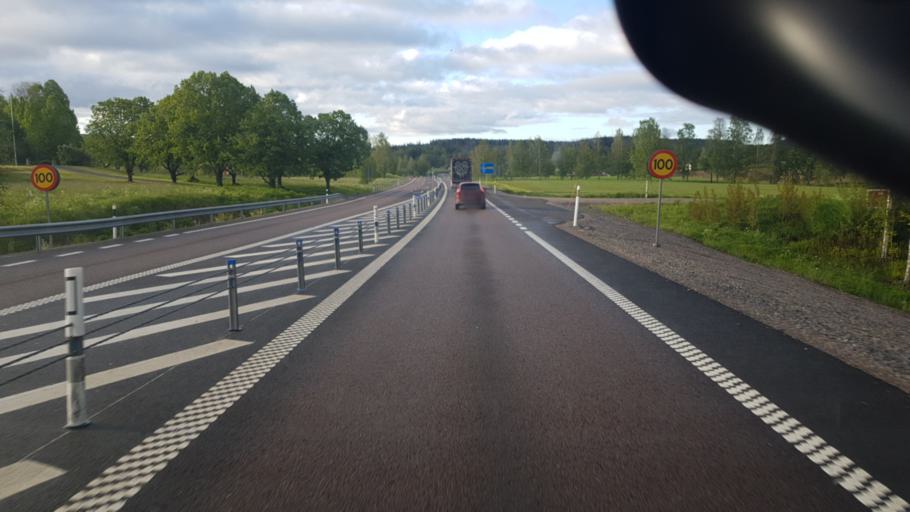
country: SE
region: Vaermland
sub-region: Eda Kommun
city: Amotfors
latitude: 59.7952
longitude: 12.3362
